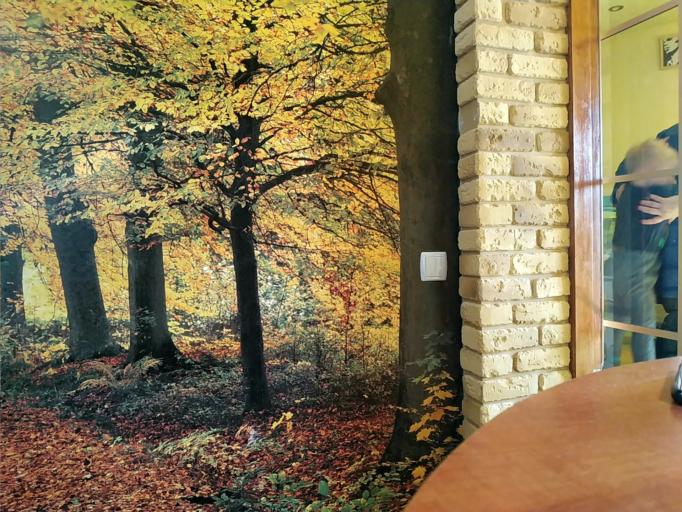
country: RU
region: Novgorod
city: Parfino
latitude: 57.8010
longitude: 31.6101
